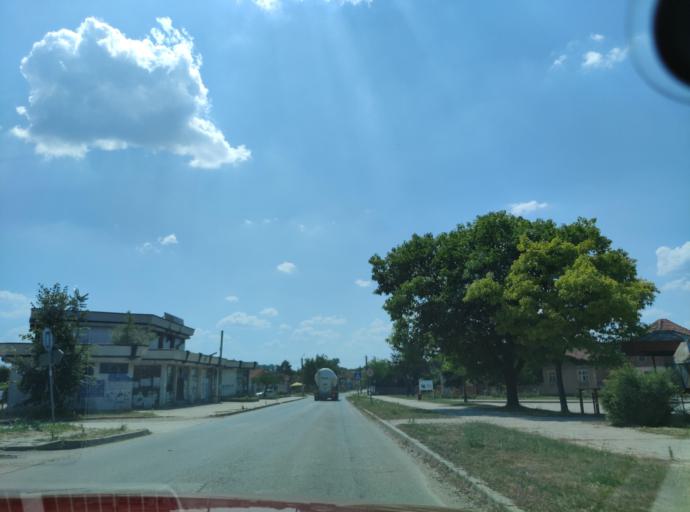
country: BG
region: Pleven
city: Iskur
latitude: 43.4547
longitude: 24.2641
